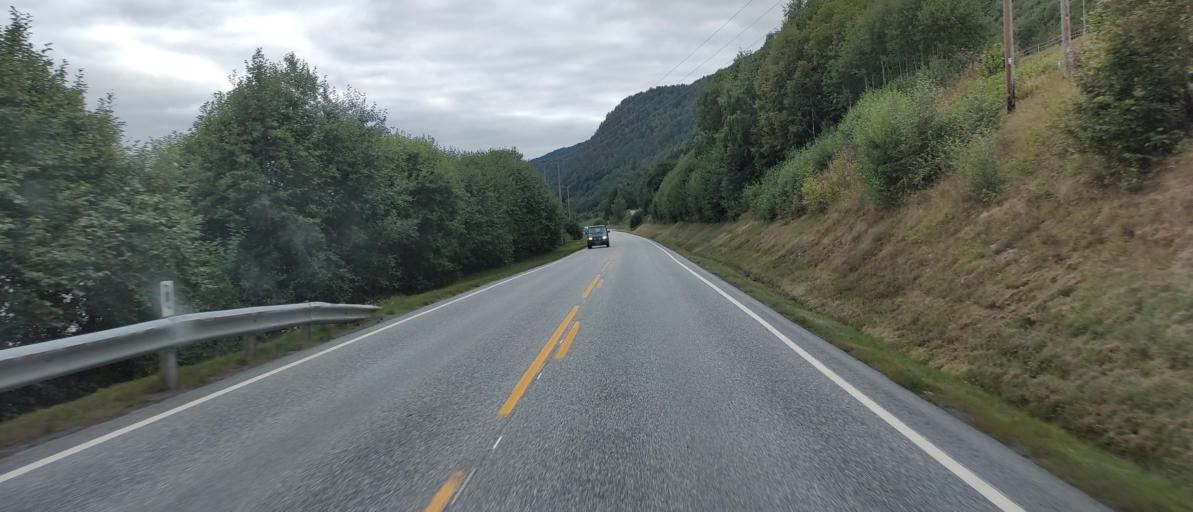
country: NO
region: More og Romsdal
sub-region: Rauma
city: Andalsnes
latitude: 62.5819
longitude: 7.7046
